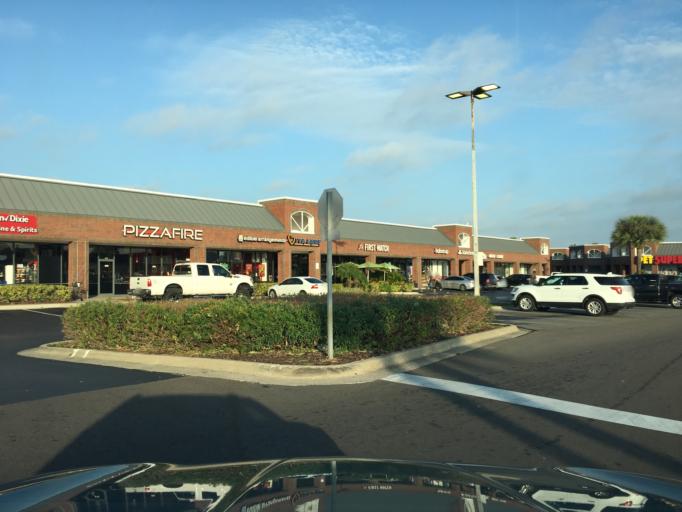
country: US
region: Florida
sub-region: Hillsborough County
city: University
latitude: 28.0553
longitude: -82.4288
